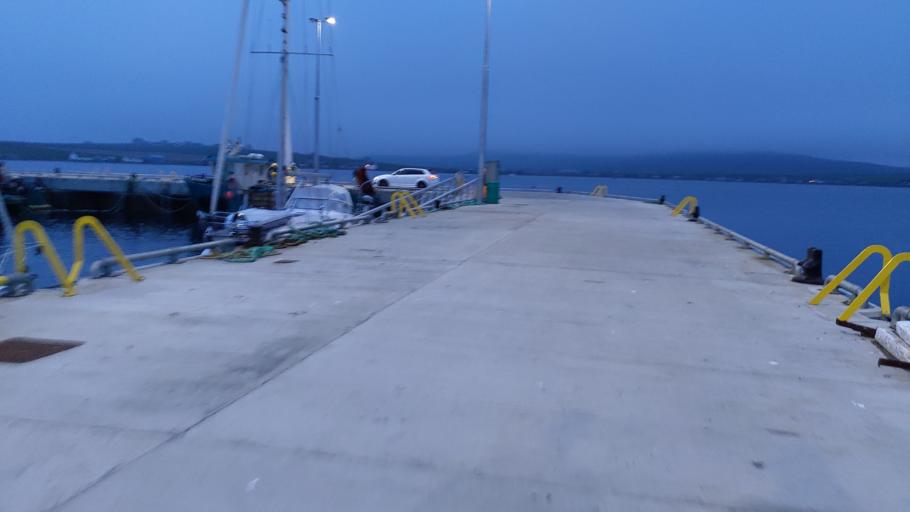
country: GB
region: Scotland
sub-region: Orkney Islands
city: Kirkwall
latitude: 59.3233
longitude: -2.9763
